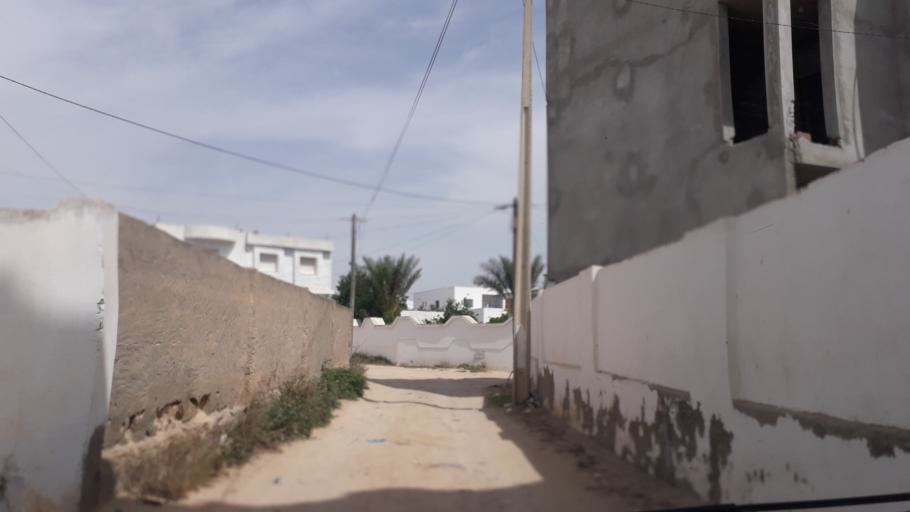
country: TN
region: Safaqis
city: Al Qarmadah
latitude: 34.8022
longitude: 10.7655
